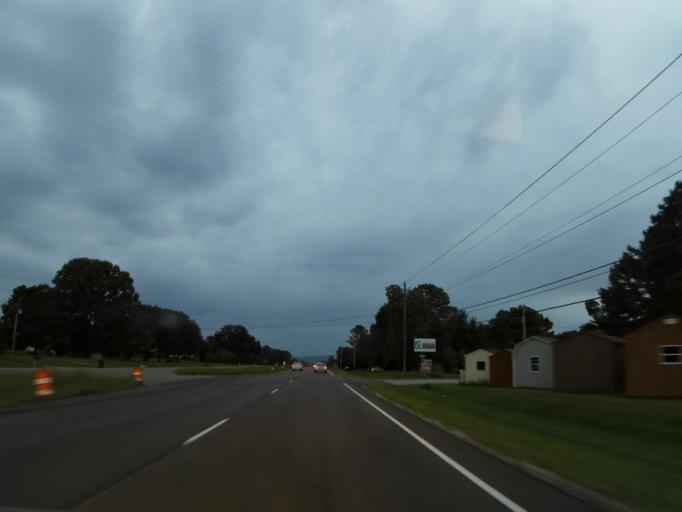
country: US
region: Alabama
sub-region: Madison County
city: Moores Mill
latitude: 34.7535
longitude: -86.4650
